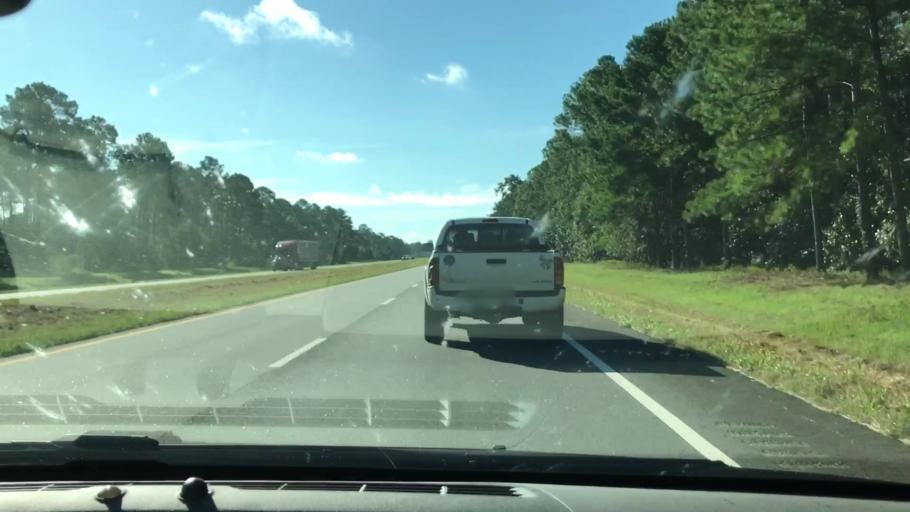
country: US
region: Georgia
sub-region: Lee County
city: Leesburg
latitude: 31.6523
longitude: -84.2663
